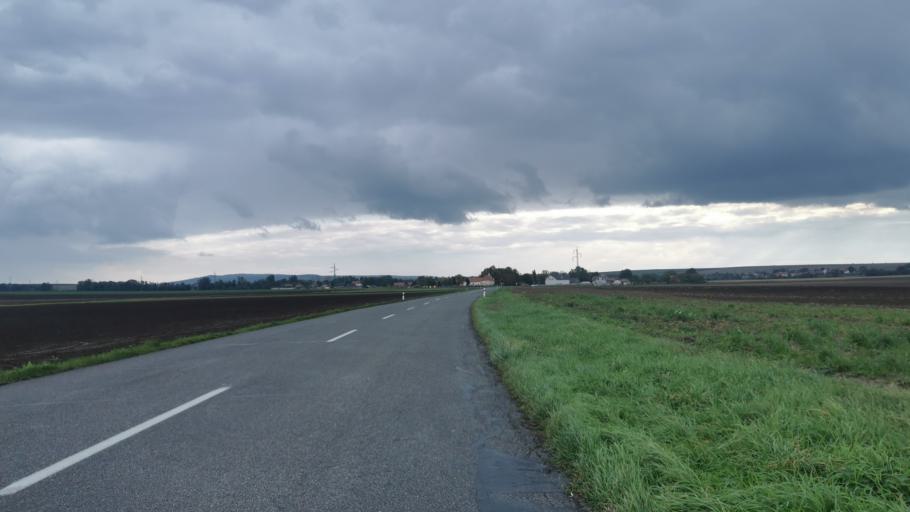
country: SK
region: Trnavsky
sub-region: Okres Skalica
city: Holic
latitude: 48.8147
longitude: 17.1942
